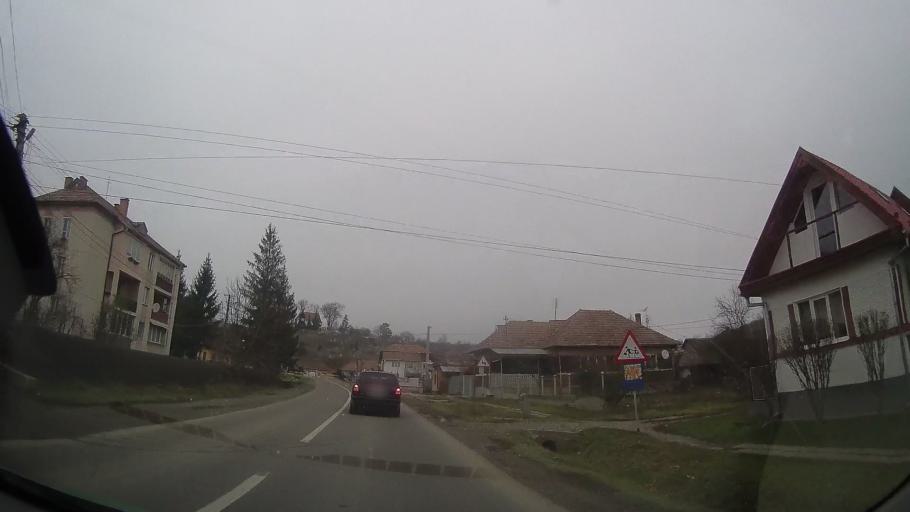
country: RO
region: Mures
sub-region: Comuna Ceausu de Campie
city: Ceausu de Campie
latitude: 46.6397
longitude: 24.5167
